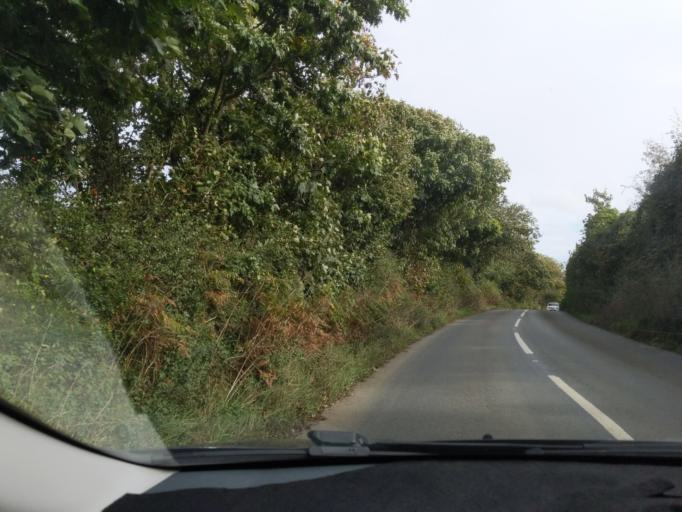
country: GB
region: England
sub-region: Cornwall
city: Mevagissey
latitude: 50.2485
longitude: -4.8176
